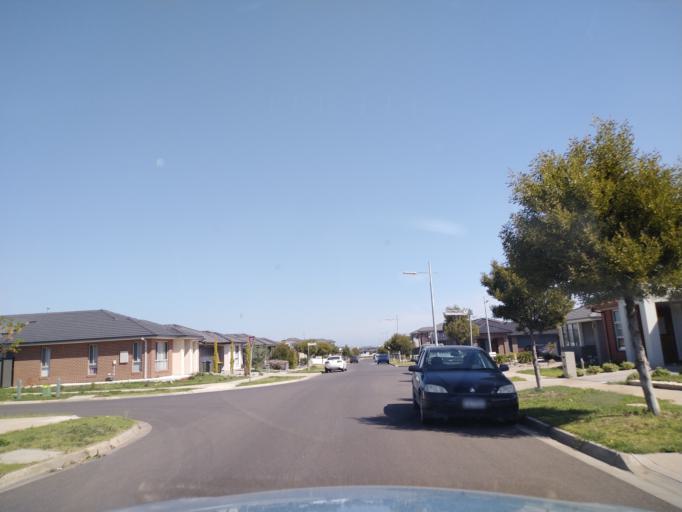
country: AU
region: Victoria
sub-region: Wyndham
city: Williams Landing
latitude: -37.8420
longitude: 144.7415
